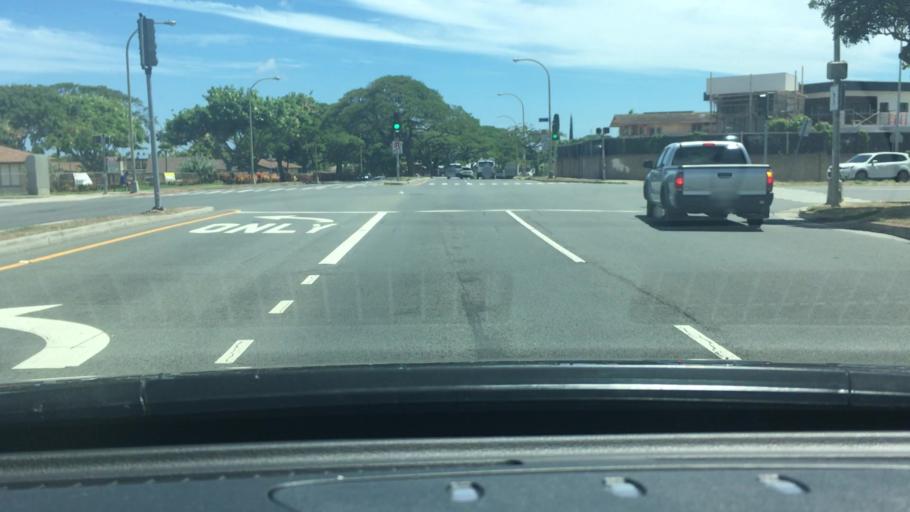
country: US
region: Hawaii
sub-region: Honolulu County
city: Honolulu
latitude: 21.2750
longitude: -157.7851
